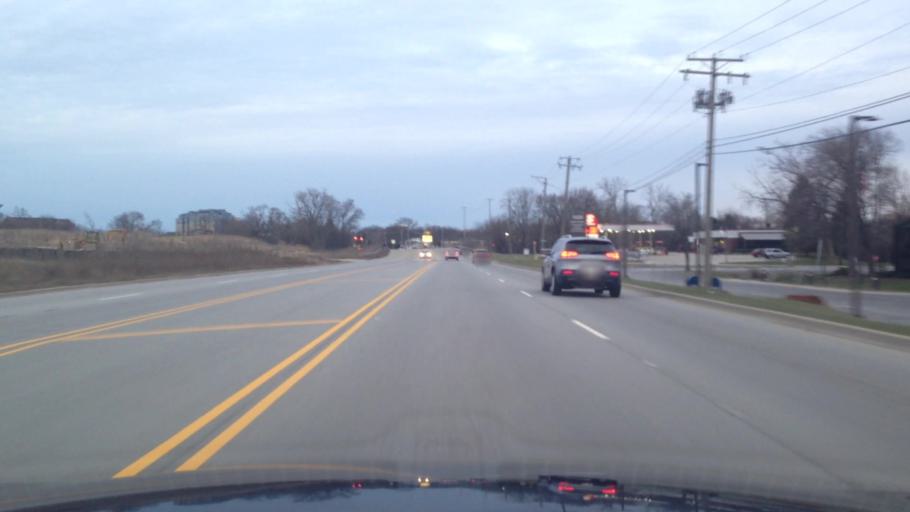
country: US
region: Illinois
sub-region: Lake County
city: Riverwoods
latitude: 42.1658
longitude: -87.9213
